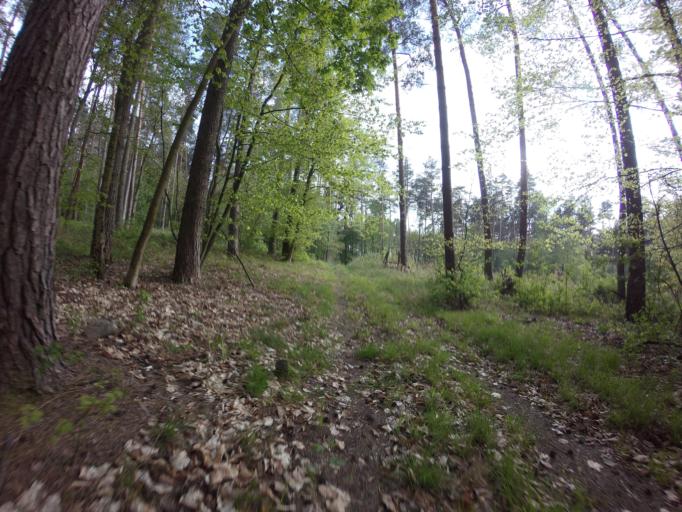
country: PL
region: West Pomeranian Voivodeship
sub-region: Powiat choszczenski
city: Choszczno
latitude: 53.1535
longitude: 15.3286
